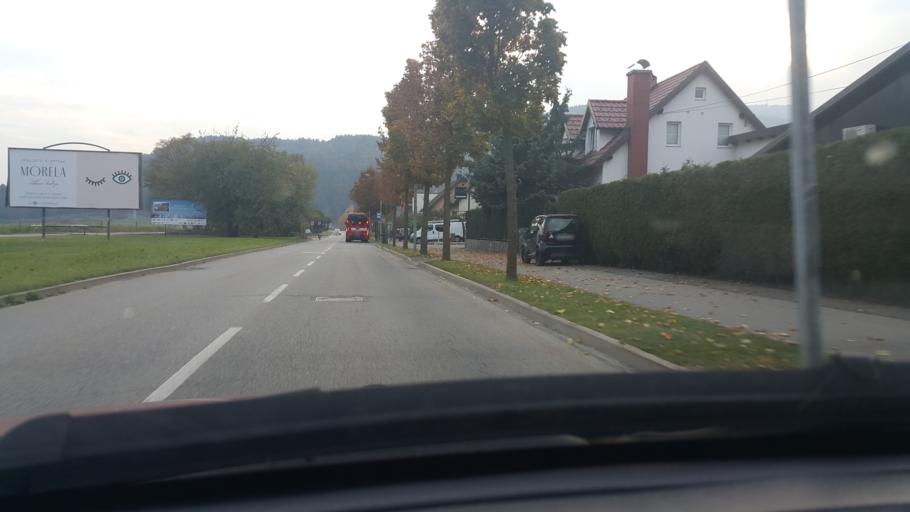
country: SI
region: Maribor
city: Razvanje
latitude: 46.5347
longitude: 15.6358
